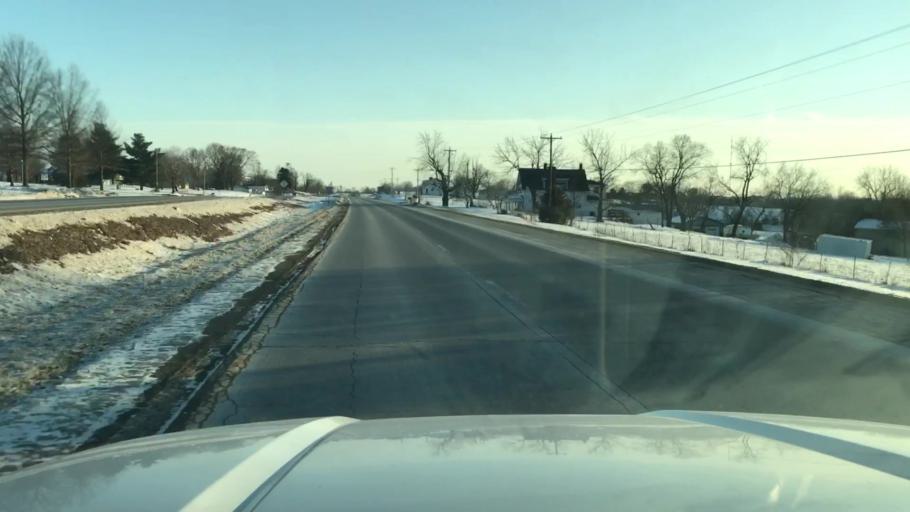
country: US
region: Missouri
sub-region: Andrew County
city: Country Club Village
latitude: 39.8747
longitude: -94.8091
